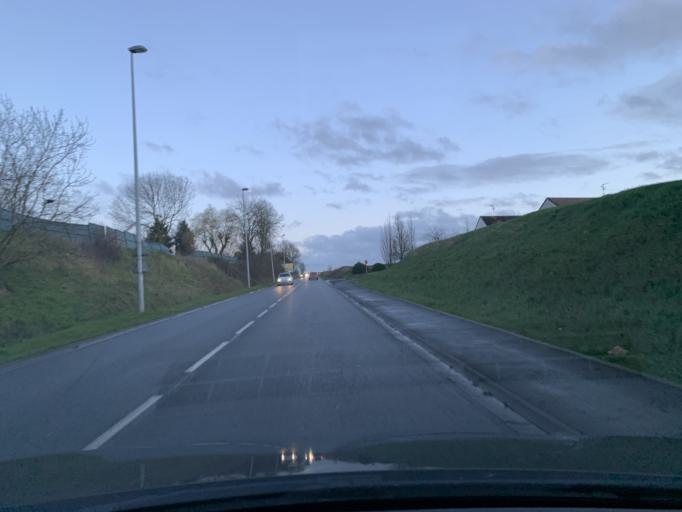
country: FR
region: Nord-Pas-de-Calais
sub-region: Departement du Nord
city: Cambrai
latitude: 50.1557
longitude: 3.2592
